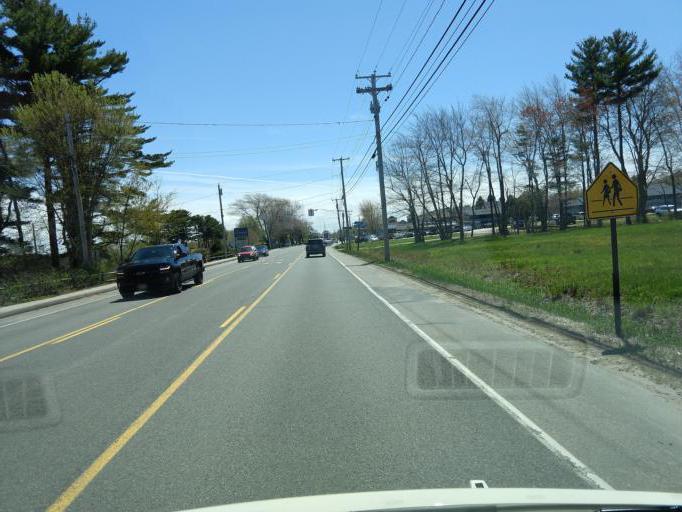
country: US
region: Maine
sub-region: York County
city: Wells Beach Station
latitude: 43.3078
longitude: -70.5848
